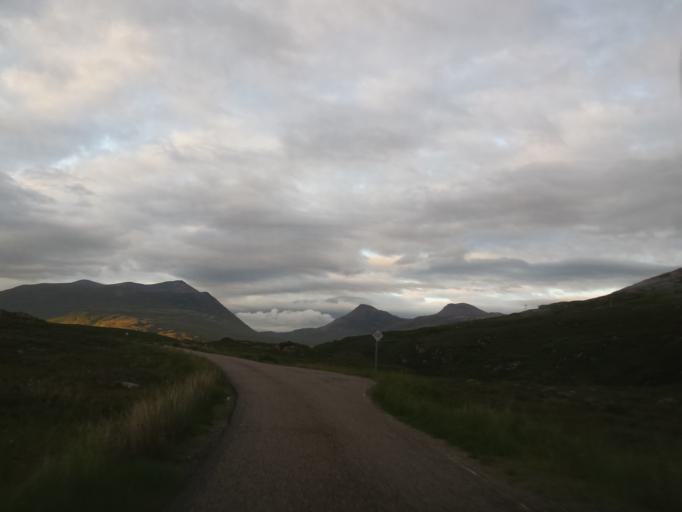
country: GB
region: Scotland
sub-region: Highland
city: Portree
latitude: 57.4359
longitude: -5.5882
